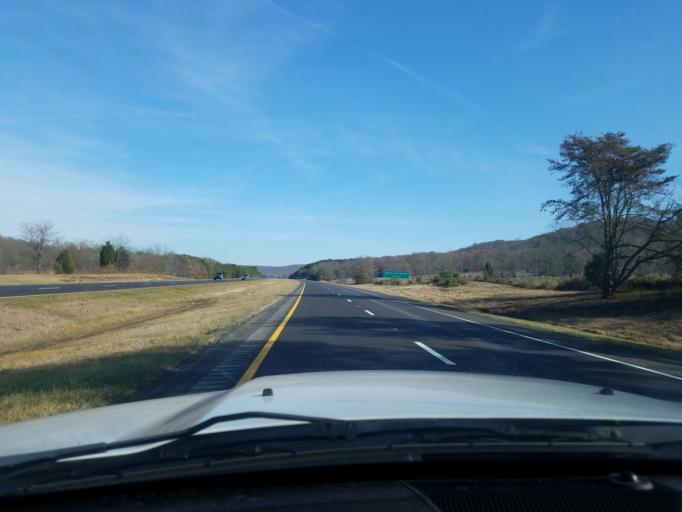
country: US
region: Ohio
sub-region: Adams County
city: Peebles
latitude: 38.9793
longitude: -83.3305
